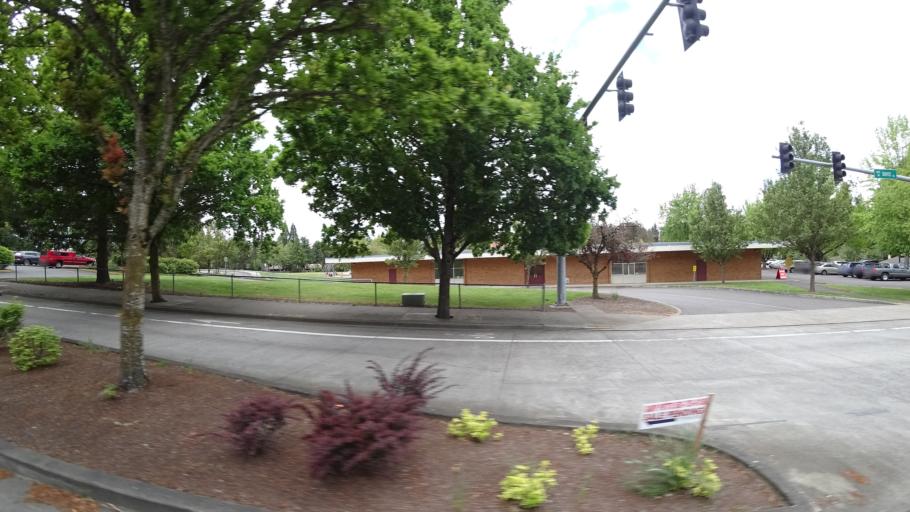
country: US
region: Oregon
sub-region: Washington County
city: Aloha
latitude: 45.4750
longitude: -122.8378
